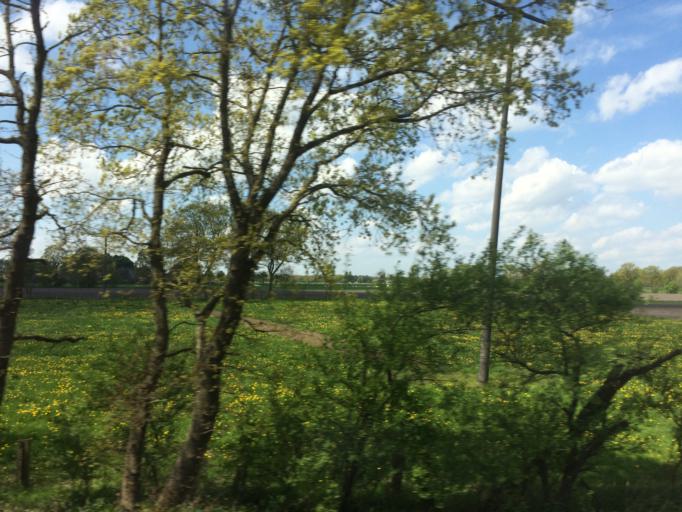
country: DE
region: Schleswig-Holstein
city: Wulfsmoor
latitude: 53.8970
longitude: 9.7183
